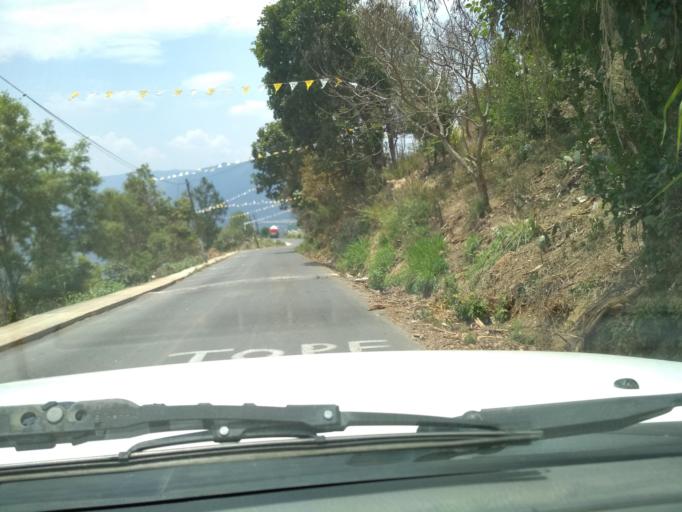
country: MX
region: Veracruz
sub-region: Acultzingo
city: Acatla
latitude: 18.7496
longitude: -97.1934
